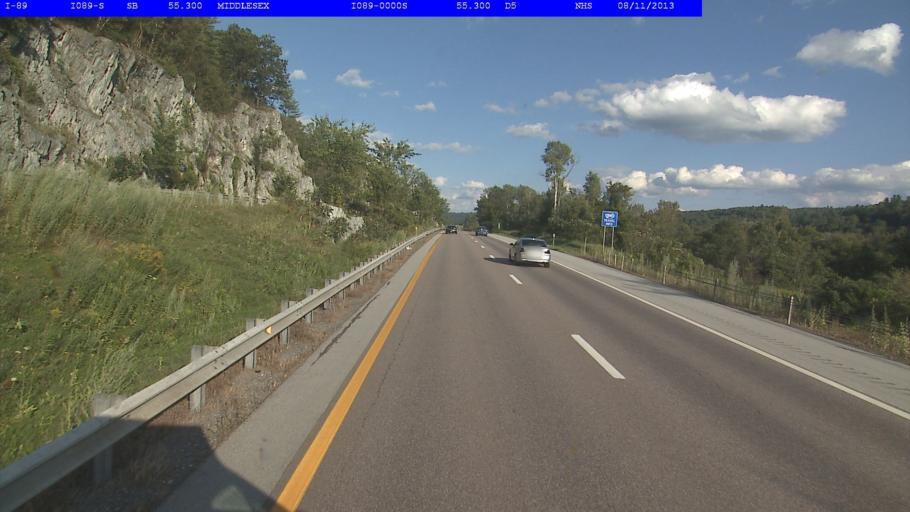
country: US
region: Vermont
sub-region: Washington County
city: Montpelier
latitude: 44.2700
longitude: -72.6316
